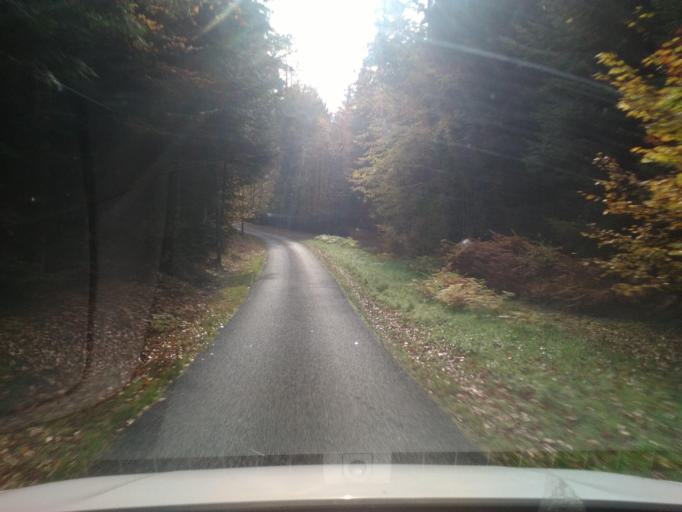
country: FR
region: Lorraine
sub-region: Departement des Vosges
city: Moyenmoutier
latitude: 48.3628
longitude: 6.8929
